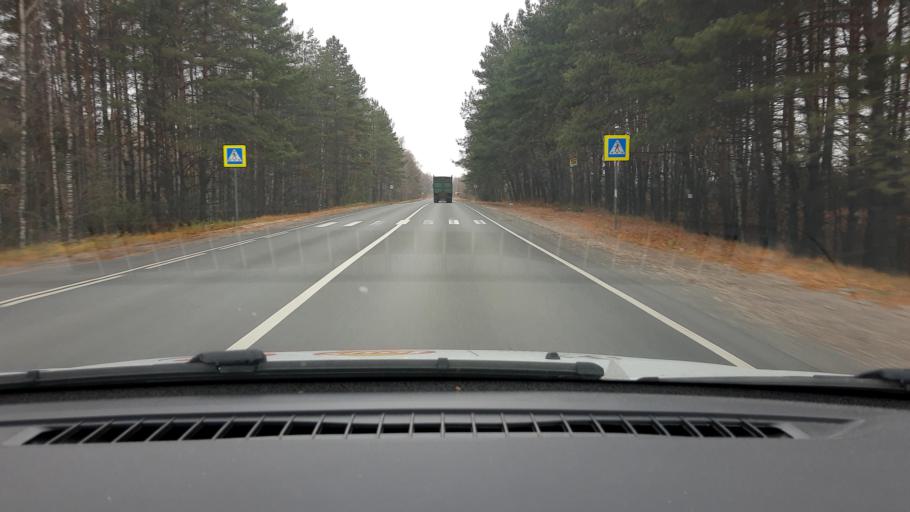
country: RU
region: Nizjnij Novgorod
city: Gidrotorf
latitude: 56.5612
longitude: 43.4948
